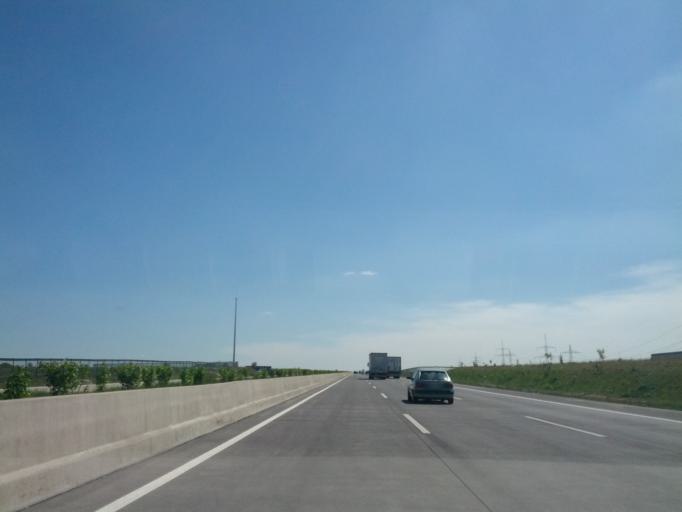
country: DE
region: Thuringia
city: Haina
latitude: 50.9931
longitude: 10.4392
